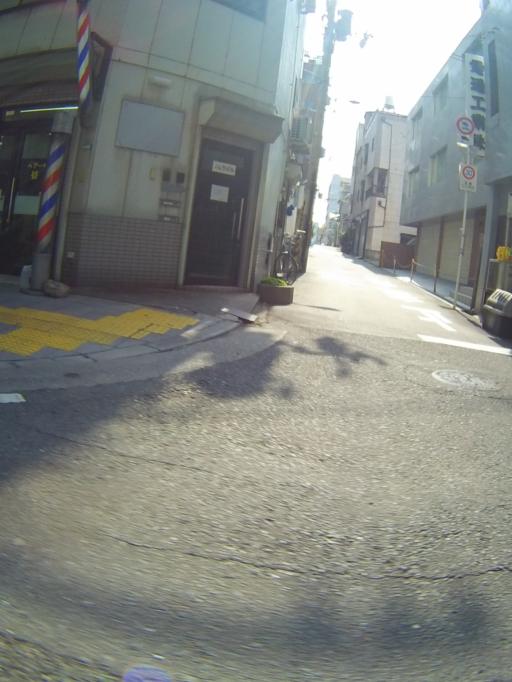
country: JP
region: Osaka
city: Osaka-shi
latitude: 34.6659
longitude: 135.4638
